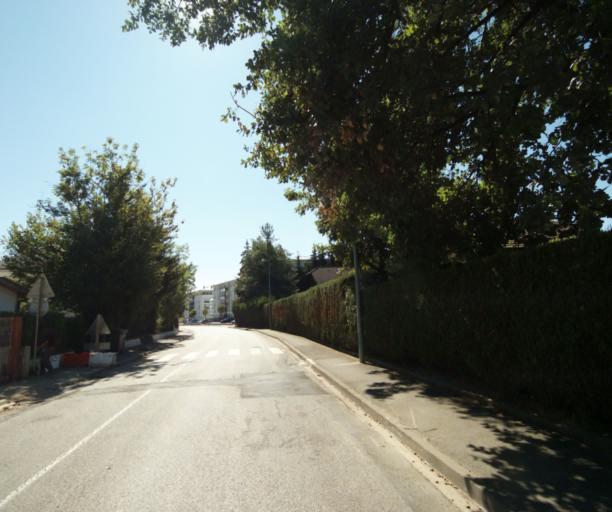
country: FR
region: Rhone-Alpes
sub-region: Departement de l'Ain
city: Ferney-Voltaire
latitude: 46.2519
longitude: 6.0978
